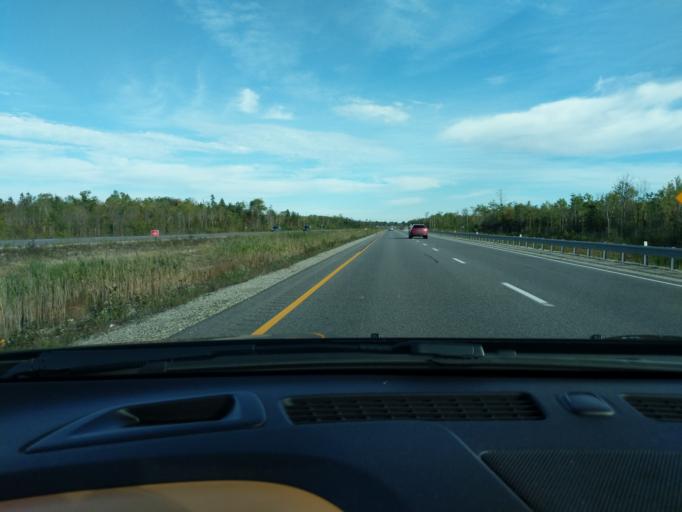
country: CA
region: Ontario
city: Collingwood
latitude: 44.4654
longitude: -80.1255
